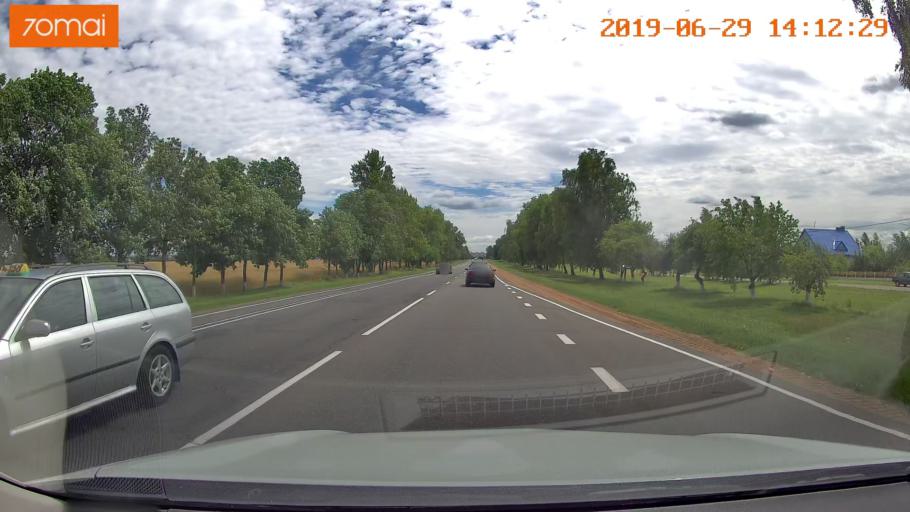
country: BY
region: Minsk
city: Salihorsk
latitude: 52.8098
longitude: 27.5076
